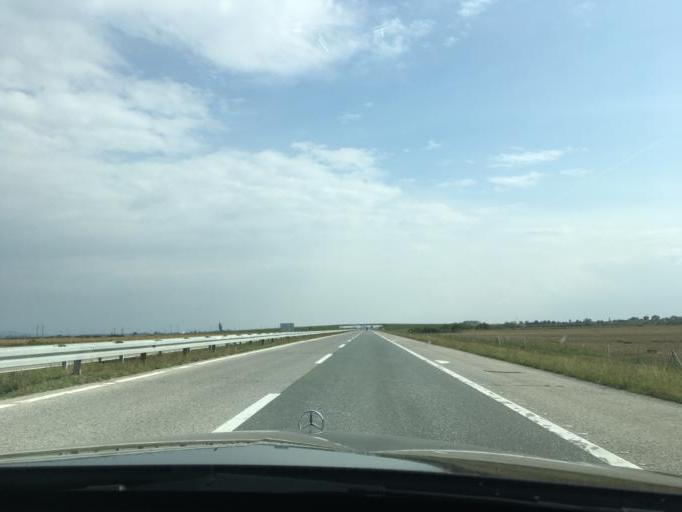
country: RS
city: Macvanska Mitrovica
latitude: 45.0181
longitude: 19.5343
